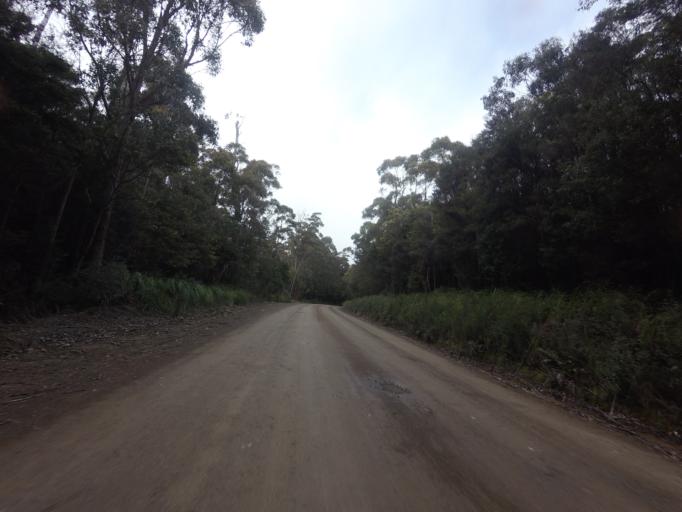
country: AU
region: Tasmania
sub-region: Huon Valley
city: Geeveston
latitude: -43.5153
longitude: 146.8860
